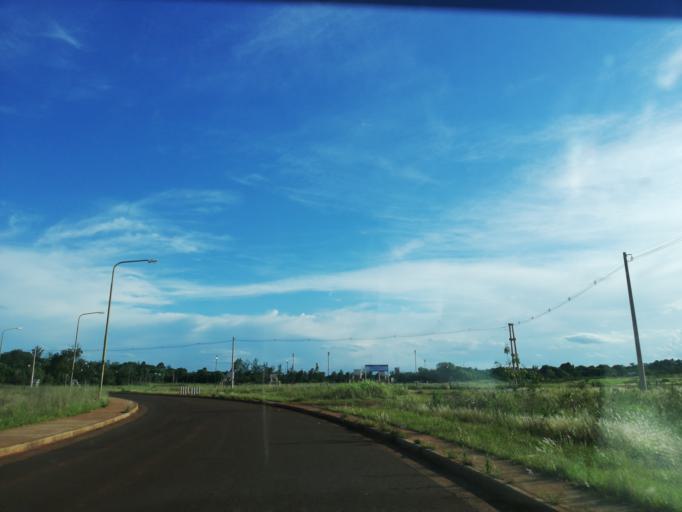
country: AR
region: Misiones
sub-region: Departamento de Capital
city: Posadas
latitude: -27.3941
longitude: -55.9562
